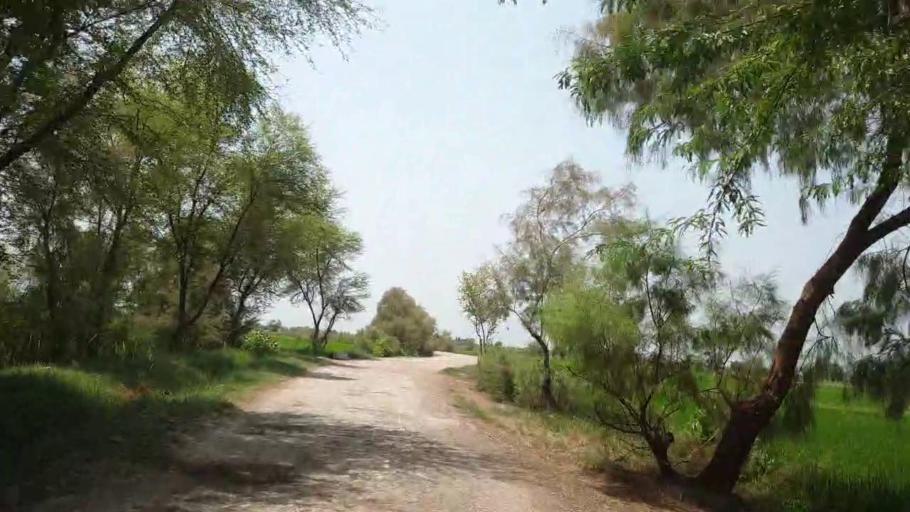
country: PK
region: Sindh
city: Shikarpur
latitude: 27.8974
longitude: 68.6321
